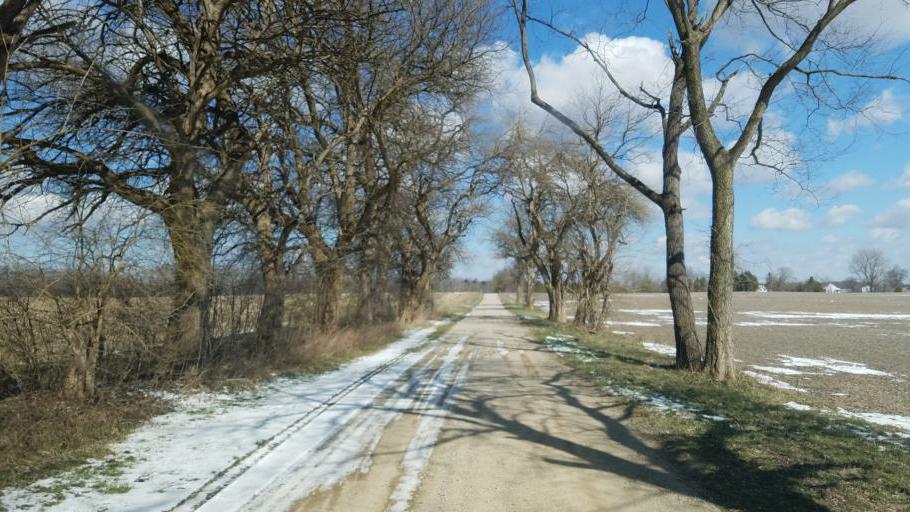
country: US
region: Ohio
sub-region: Licking County
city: Utica
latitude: 40.2609
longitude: -82.4999
